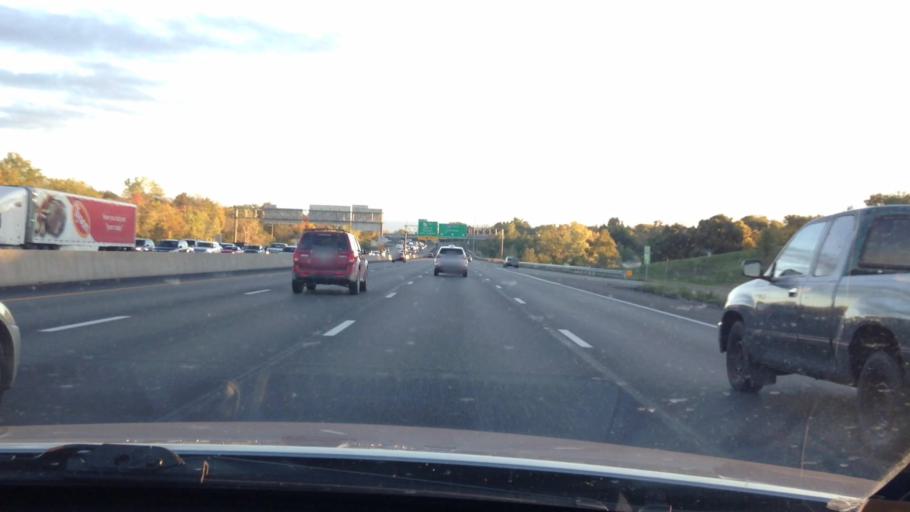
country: US
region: Missouri
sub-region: Jackson County
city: Raytown
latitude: 39.0291
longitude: -94.5008
